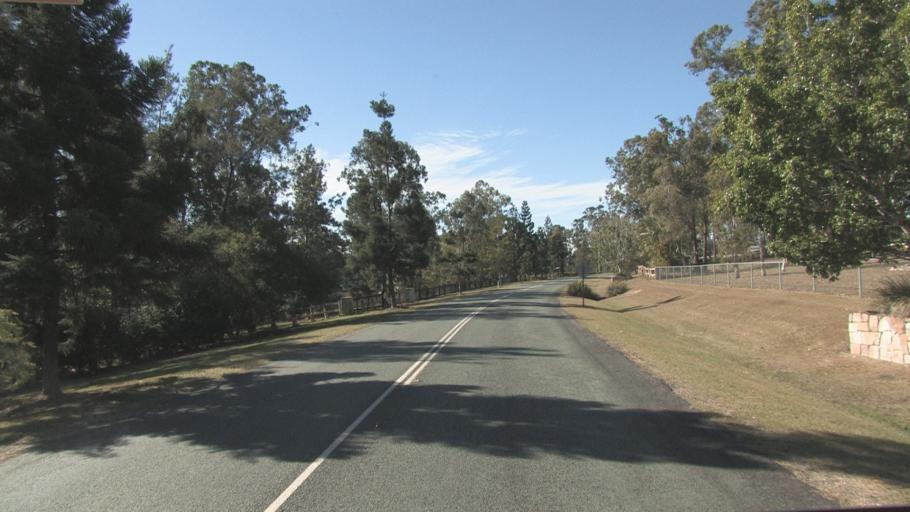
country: AU
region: Queensland
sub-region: Ipswich
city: Springfield Lakes
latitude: -27.7310
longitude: 152.9255
